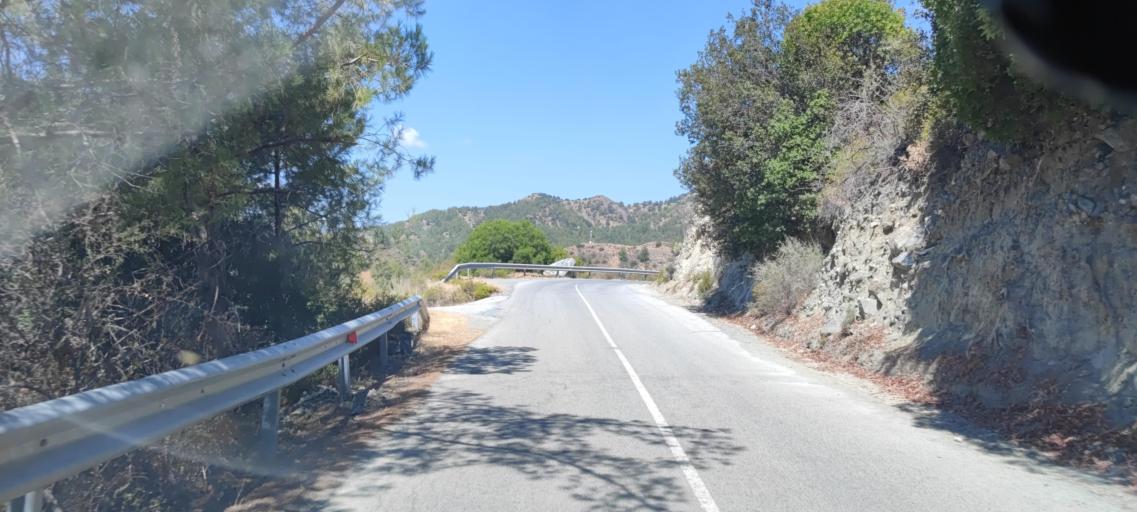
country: CY
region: Lefkosia
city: Kakopetria
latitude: 34.9236
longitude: 32.7949
